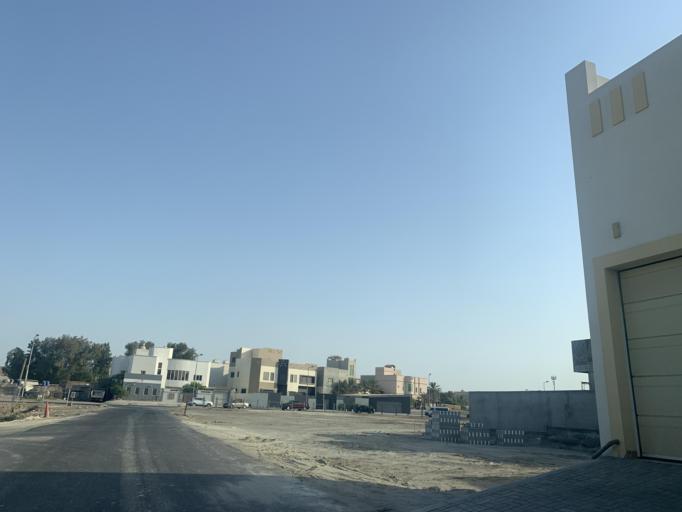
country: BH
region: Muharraq
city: Al Muharraq
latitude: 26.2869
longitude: 50.6332
